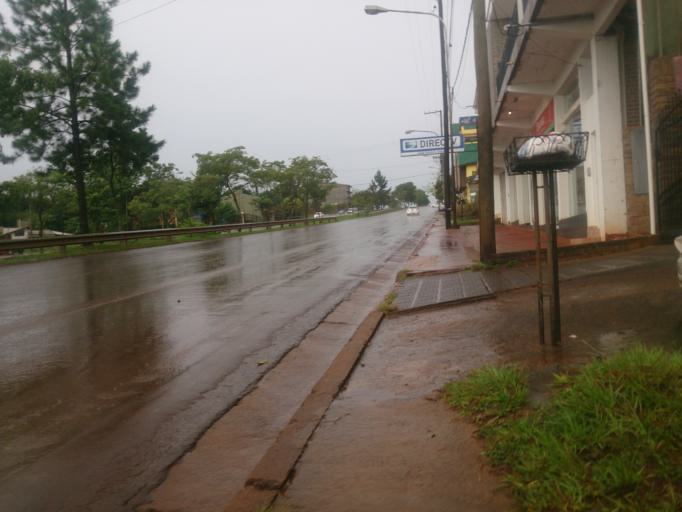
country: AR
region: Misiones
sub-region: Departamento de Obera
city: Obera
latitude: -27.4783
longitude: -55.1025
